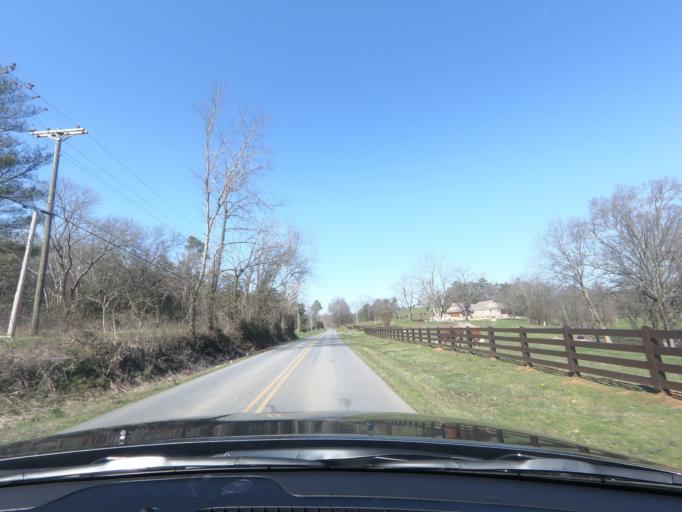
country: US
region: Georgia
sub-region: Bartow County
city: Rydal
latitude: 34.4377
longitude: -84.8068
